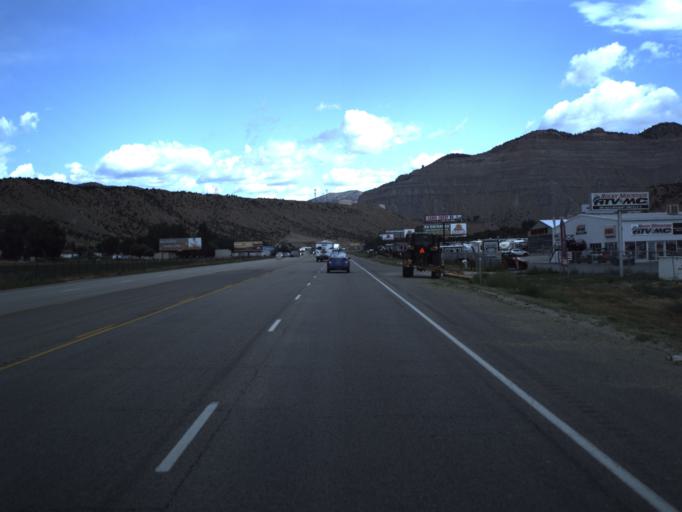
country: US
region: Utah
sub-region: Carbon County
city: Spring Glen
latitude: 39.6659
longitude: -110.8611
